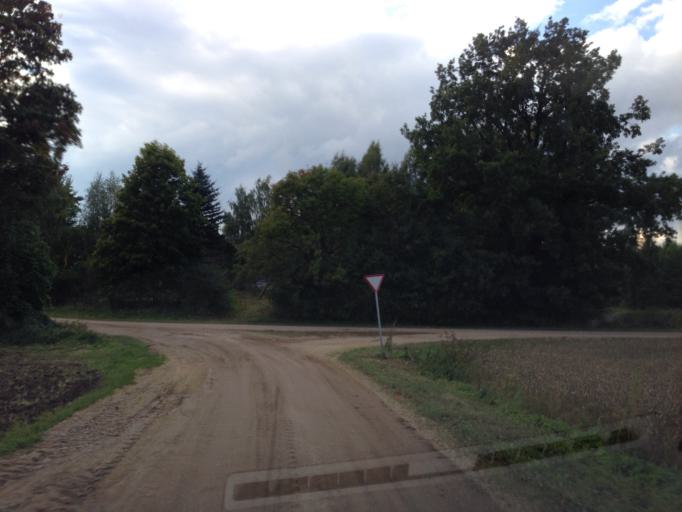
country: EE
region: Tartu
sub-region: Puhja vald
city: Puhja
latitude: 58.1914
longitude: 26.1992
